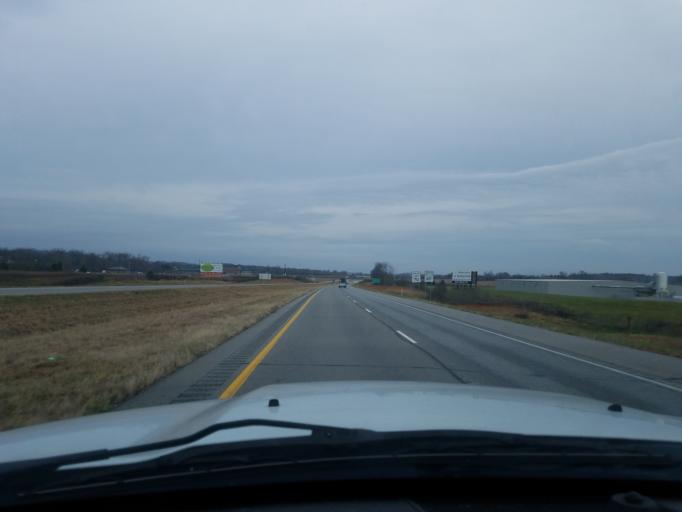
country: US
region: Indiana
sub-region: Harrison County
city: Corydon
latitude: 38.2392
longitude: -86.1385
